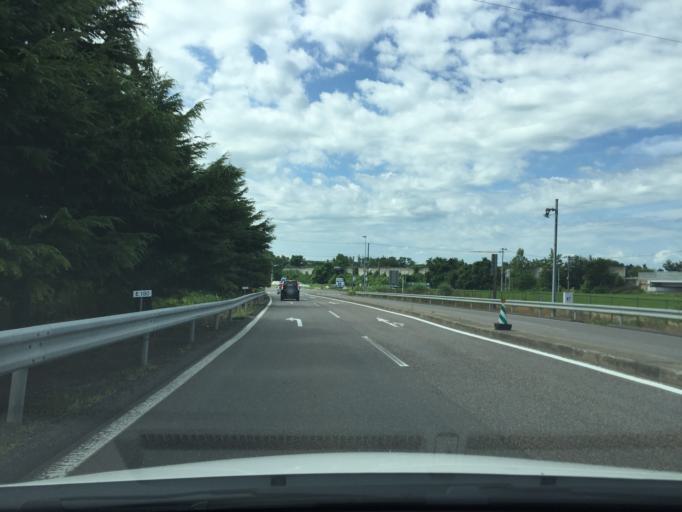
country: JP
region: Fukushima
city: Koriyama
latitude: 37.3635
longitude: 140.3142
